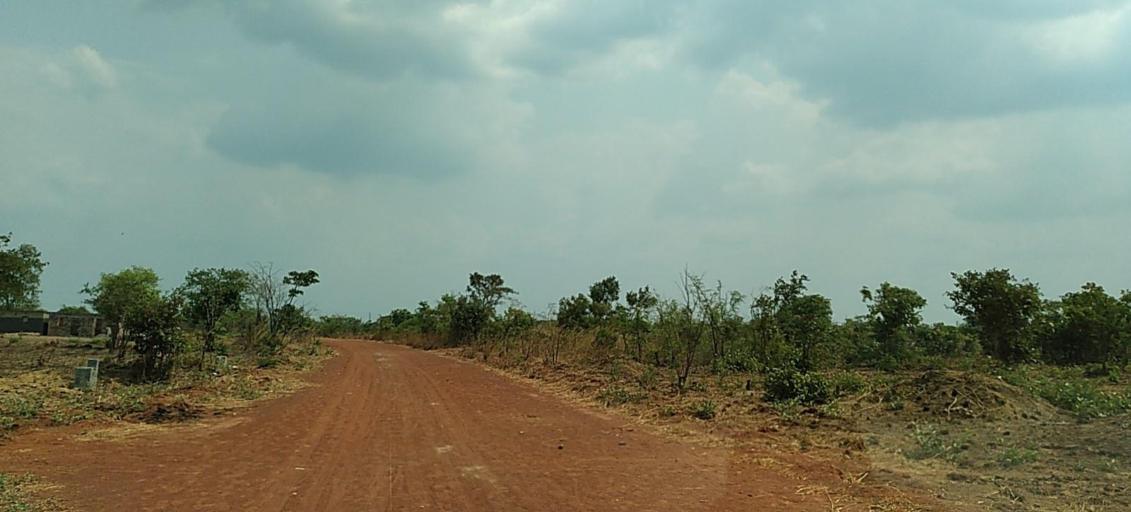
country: ZM
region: Copperbelt
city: Kalulushi
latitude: -12.8781
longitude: 28.0746
